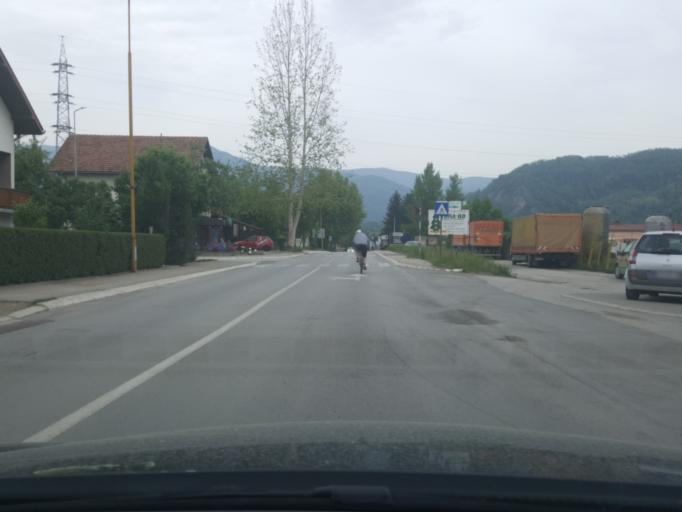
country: RS
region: Central Serbia
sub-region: Zlatiborski Okrug
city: Bajina Basta
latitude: 43.9785
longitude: 19.5689
